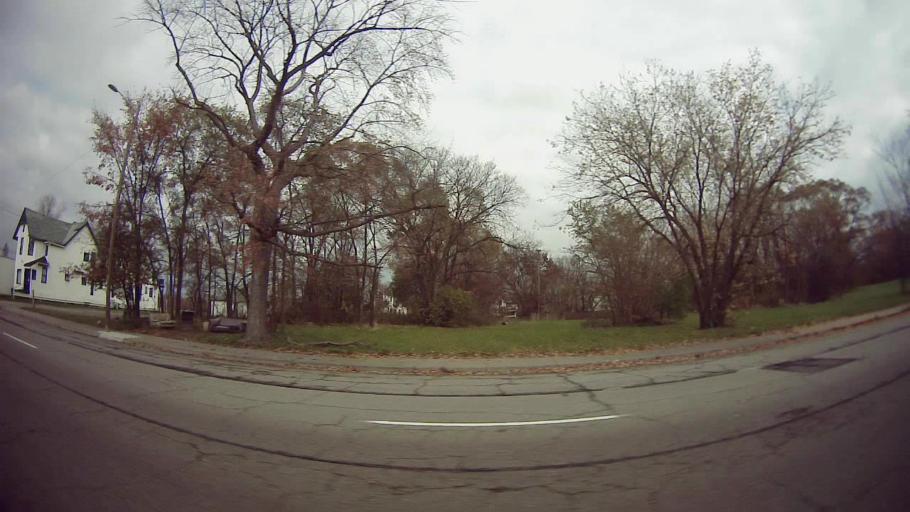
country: US
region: Michigan
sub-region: Wayne County
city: Detroit
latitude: 42.3446
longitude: -83.0840
